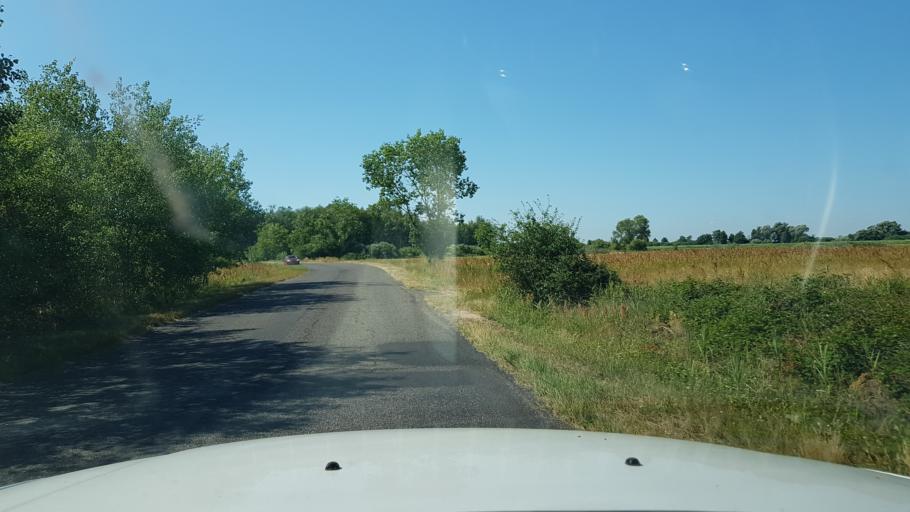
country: PL
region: West Pomeranian Voivodeship
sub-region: Powiat goleniowski
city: Goleniow
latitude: 53.4712
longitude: 14.7164
